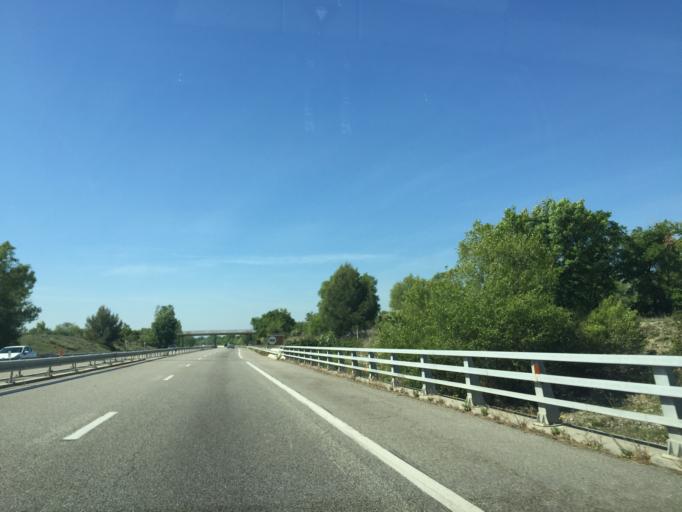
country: FR
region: Provence-Alpes-Cote d'Azur
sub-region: Departement des Alpes-de-Haute-Provence
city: Villeneuve
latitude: 43.8698
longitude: 5.8711
